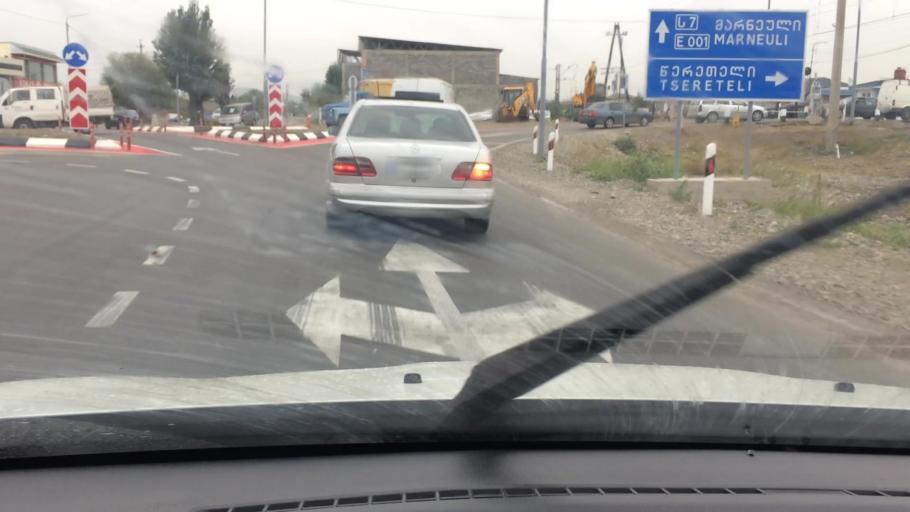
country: GE
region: Kvemo Kartli
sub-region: Marneuli
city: Marneuli
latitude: 41.4599
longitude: 44.8103
